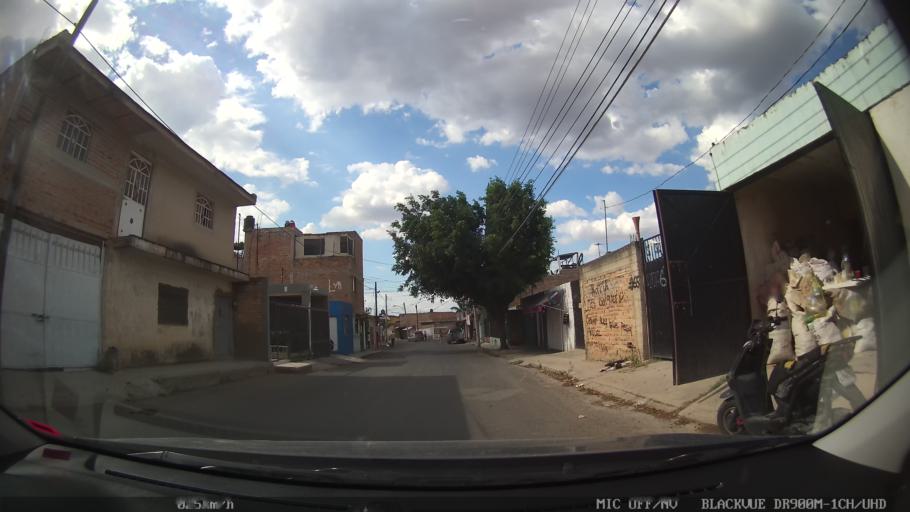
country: MX
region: Jalisco
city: Tlaquepaque
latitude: 20.6605
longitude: -103.2628
